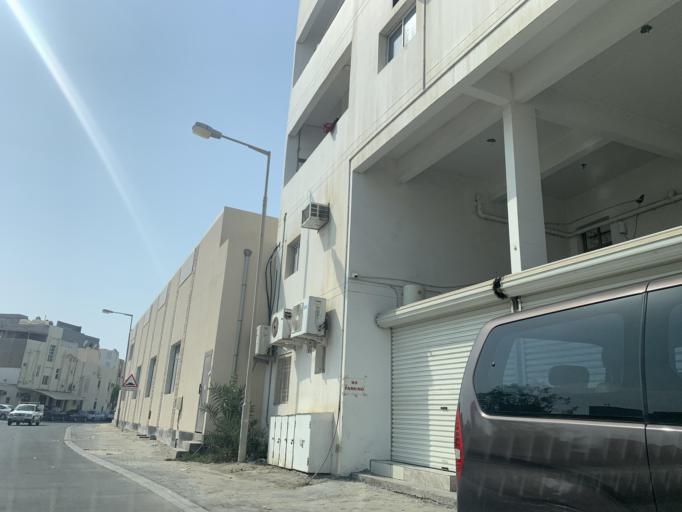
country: BH
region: Muharraq
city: Al Hadd
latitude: 26.2724
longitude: 50.6539
